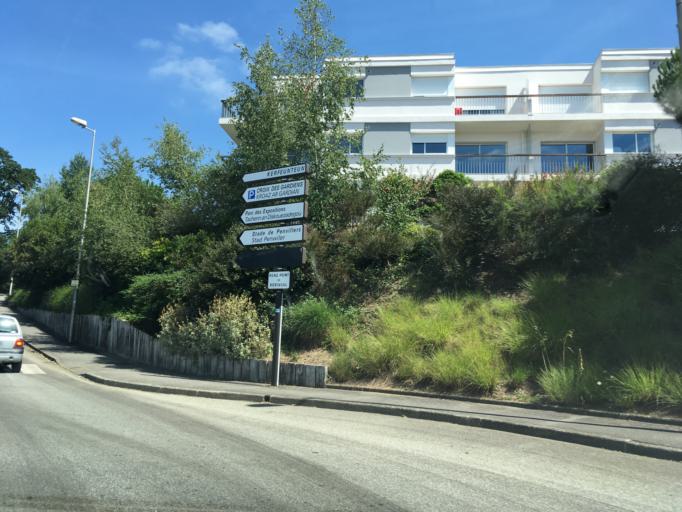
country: FR
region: Brittany
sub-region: Departement du Finistere
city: Quimper
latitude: 48.0064
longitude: -4.1075
